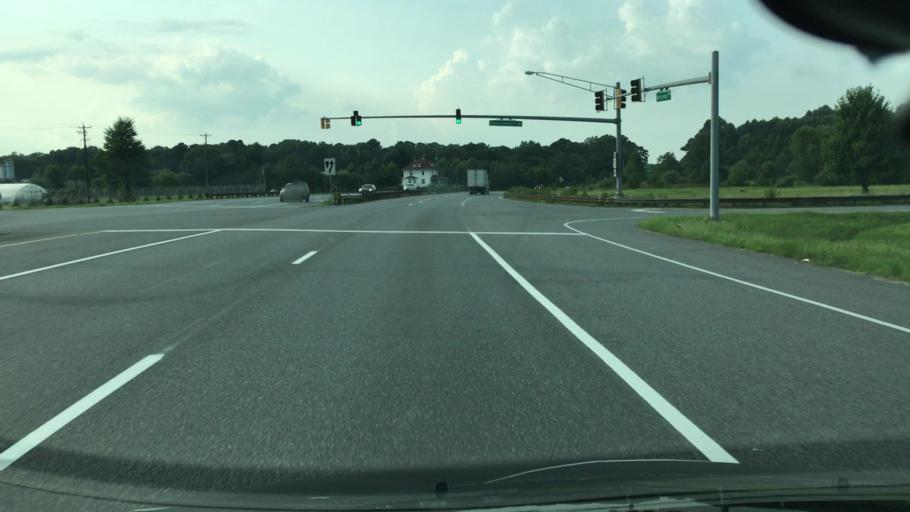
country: US
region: Delaware
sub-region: Sussex County
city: Selbyville
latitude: 38.4050
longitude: -75.2119
